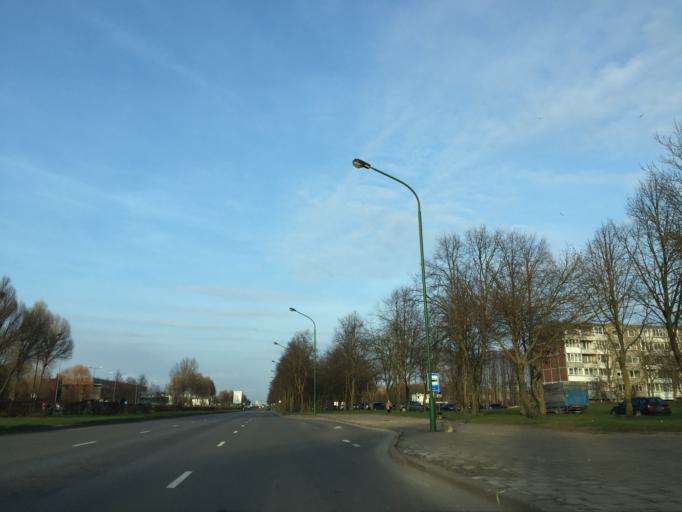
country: LT
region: Klaipedos apskritis
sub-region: Klaipeda
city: Klaipeda
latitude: 55.6878
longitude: 21.1635
